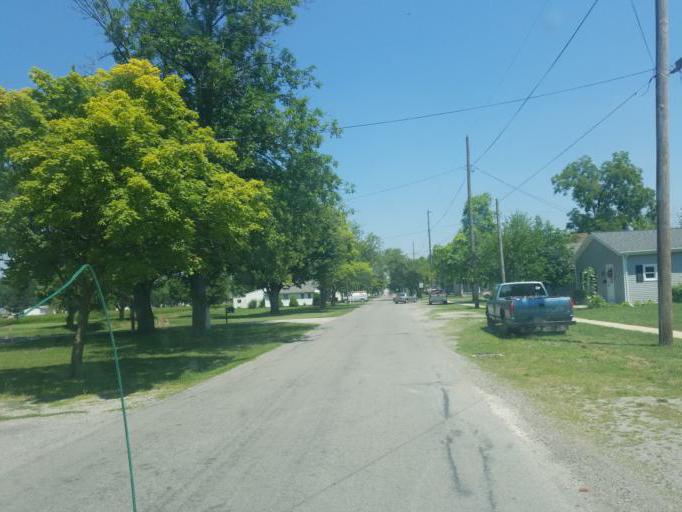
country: US
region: Ohio
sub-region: Allen County
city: Spencerville
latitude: 40.7102
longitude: -84.3563
